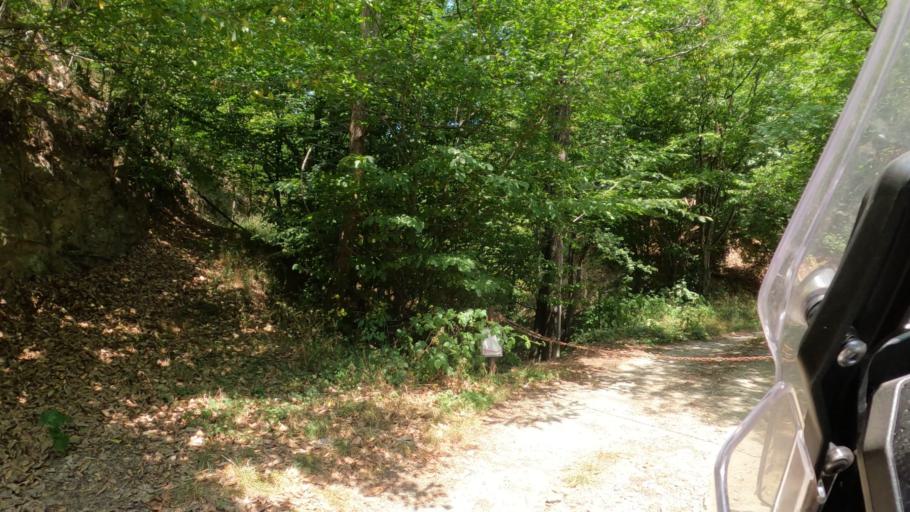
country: IT
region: Piedmont
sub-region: Provincia di Alessandria
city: Cassinelle-Concentrico
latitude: 44.5679
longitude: 8.5674
